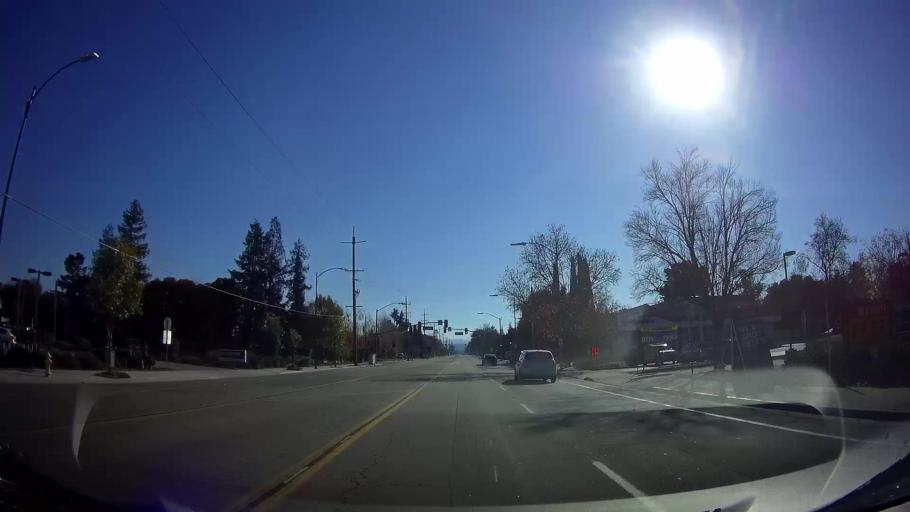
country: US
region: California
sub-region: Santa Clara County
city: Seven Trees
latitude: 37.2734
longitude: -121.8695
